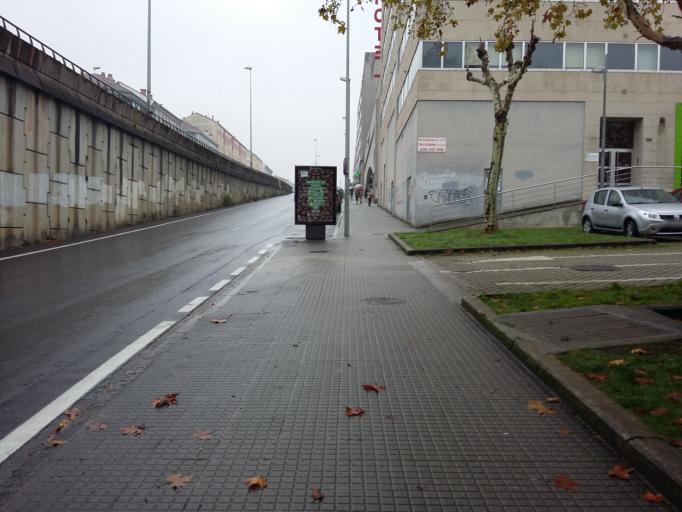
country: ES
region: Galicia
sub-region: Provincia da Coruna
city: Santiago de Compostela
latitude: 42.8658
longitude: -8.5442
